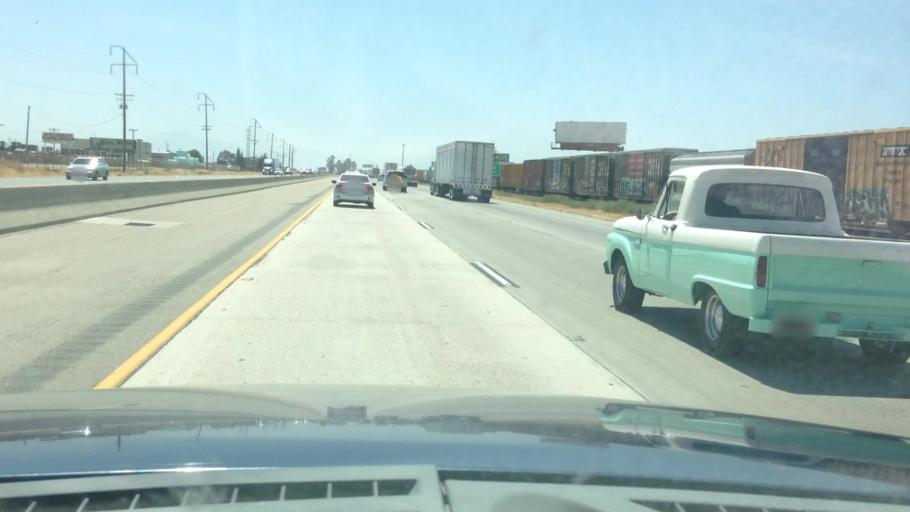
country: US
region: California
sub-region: Kern County
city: Greenacres
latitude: 35.4499
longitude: -119.0985
